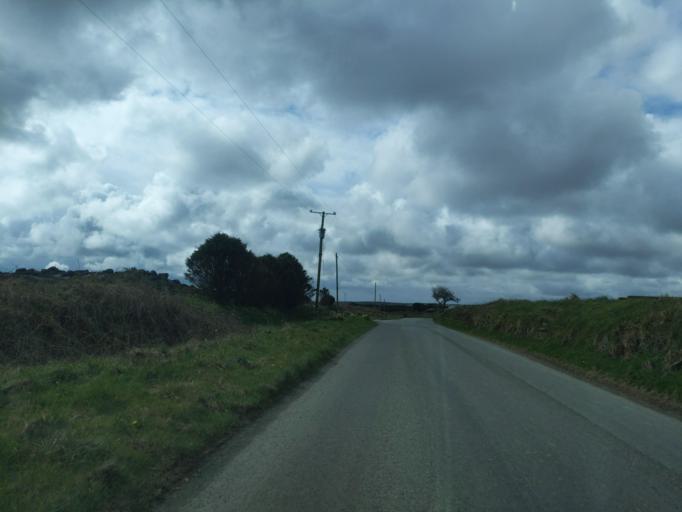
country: GB
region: England
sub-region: Cornwall
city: Camelford
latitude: 50.6409
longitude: -4.6416
